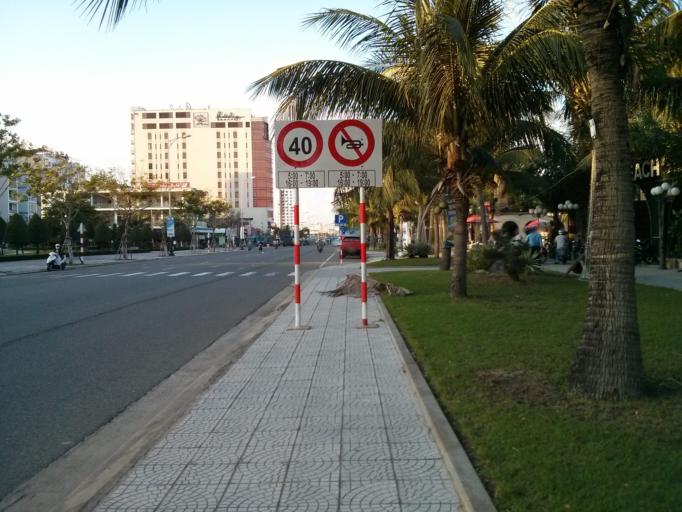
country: VN
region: Da Nang
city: Son Tra
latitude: 16.0477
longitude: 108.2495
